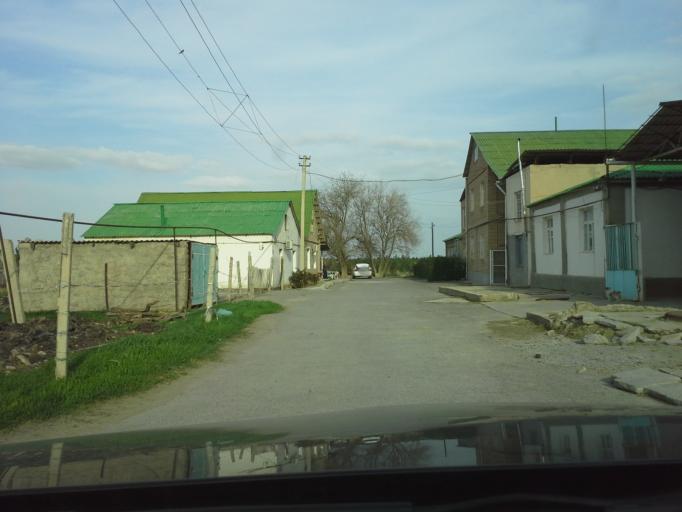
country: TM
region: Ahal
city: Abadan
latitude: 37.9321
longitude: 58.2320
